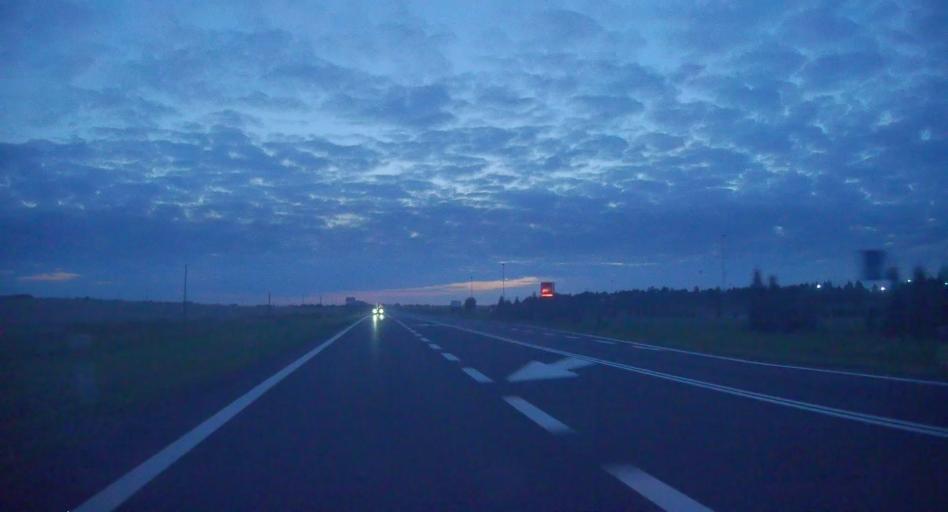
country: PL
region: Silesian Voivodeship
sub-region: Powiat klobucki
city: Klobuck
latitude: 50.8864
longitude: 18.9782
